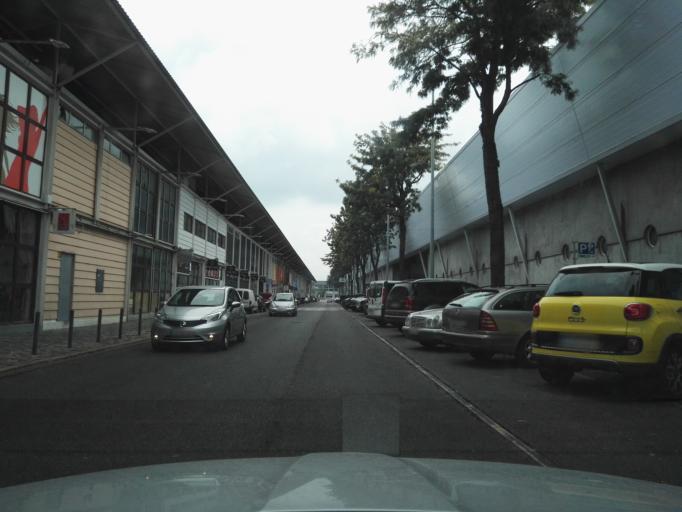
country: PT
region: Lisbon
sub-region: Loures
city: Moscavide
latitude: 38.7723
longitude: -9.0925
